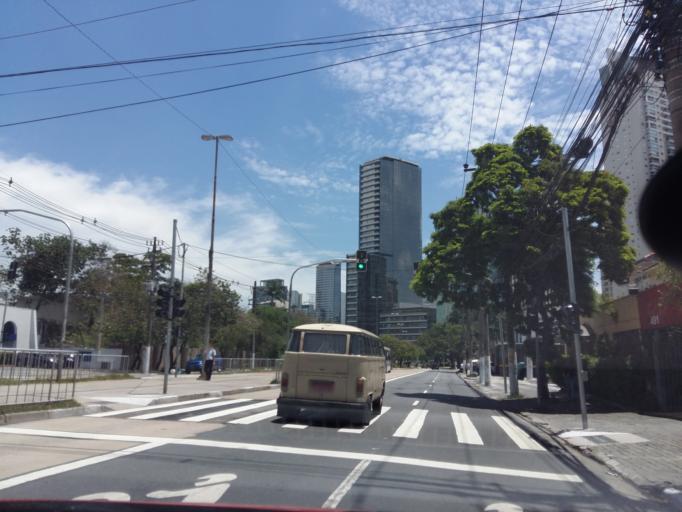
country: BR
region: Sao Paulo
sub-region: Sao Paulo
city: Sao Paulo
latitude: -23.6012
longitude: -46.6914
